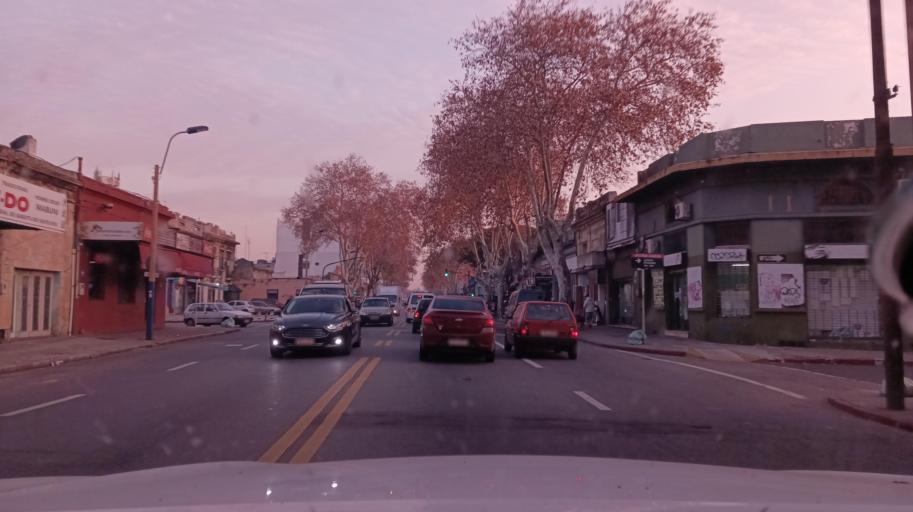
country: UY
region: Montevideo
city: Montevideo
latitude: -34.8727
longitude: -56.1766
